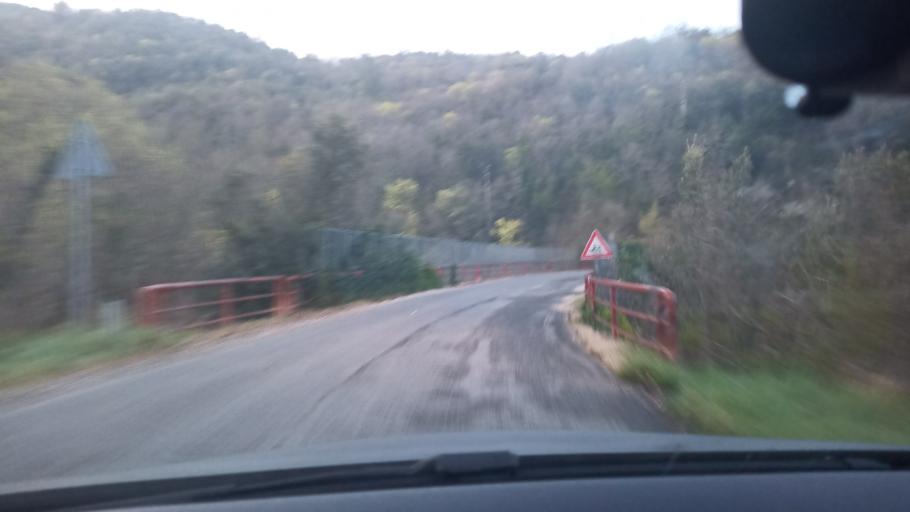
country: IT
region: Latium
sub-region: Provincia di Rieti
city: Cottanello
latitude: 42.4028
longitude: 12.6820
